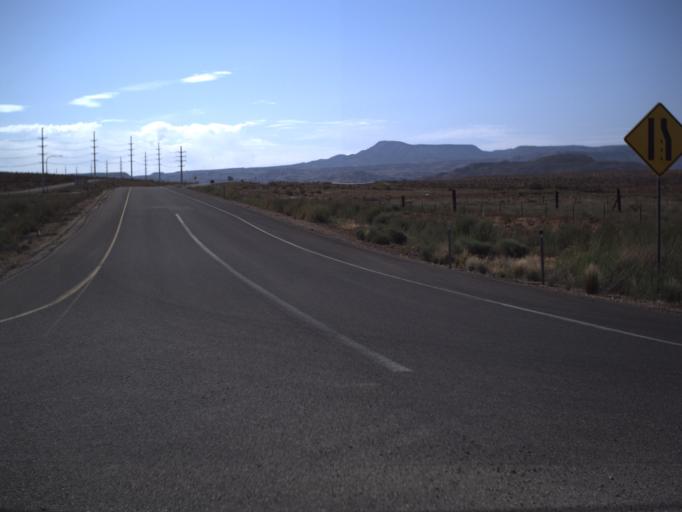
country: US
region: Utah
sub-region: Washington County
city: Washington
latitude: 37.0593
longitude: -113.4867
